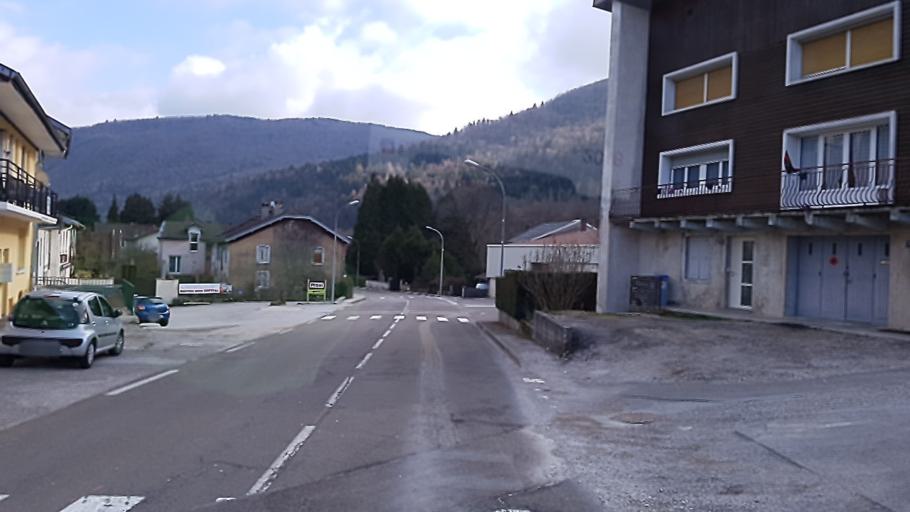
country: FR
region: Franche-Comte
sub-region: Departement du Jura
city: Lavans-les-Saint-Claude
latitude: 46.3591
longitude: 5.7340
